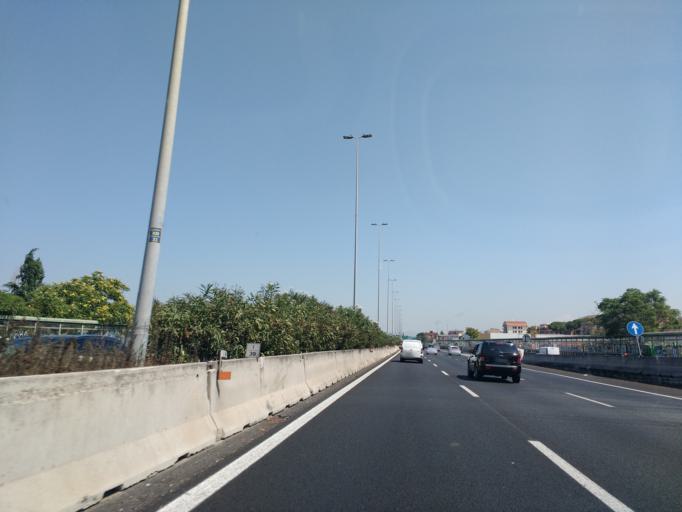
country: IT
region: Latium
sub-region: Citta metropolitana di Roma Capitale
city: Ciampino
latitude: 41.8555
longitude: 12.5981
